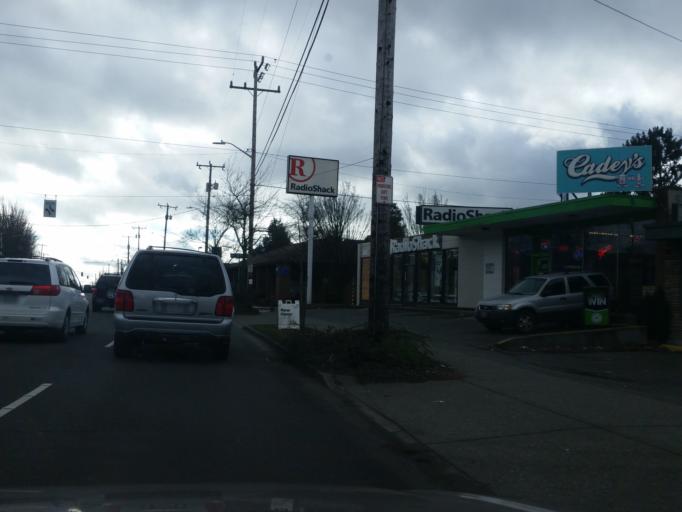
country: US
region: Washington
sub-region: King County
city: Shoreline
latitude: 47.6929
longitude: -122.3768
